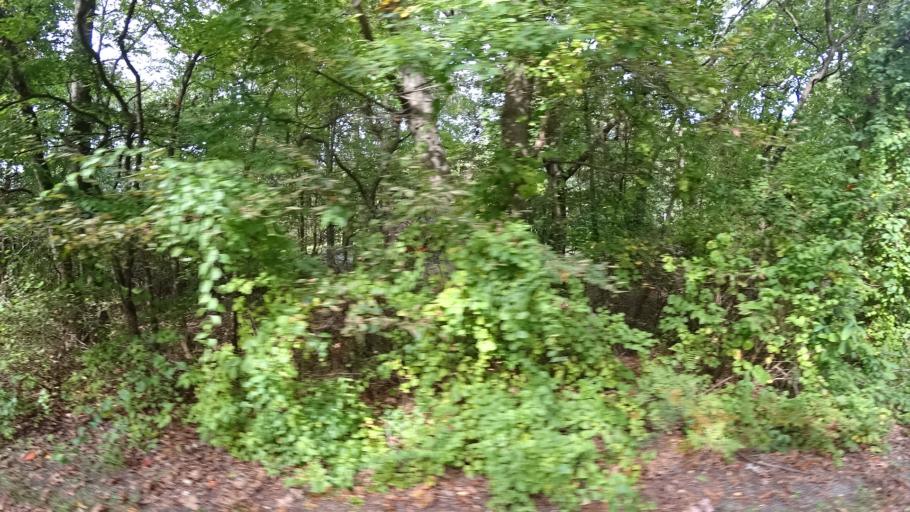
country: US
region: Indiana
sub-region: LaPorte County
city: Long Beach
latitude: 41.7349
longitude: -86.8463
